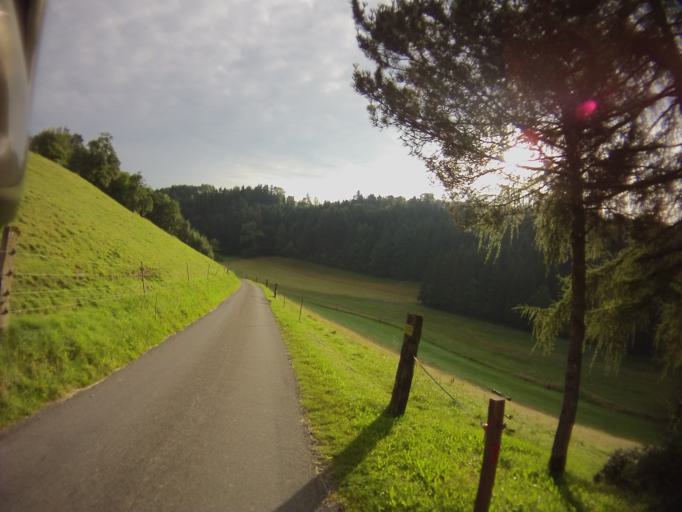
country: CH
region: Zug
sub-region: Zug
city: Steinhausen
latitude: 47.2164
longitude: 8.4842
